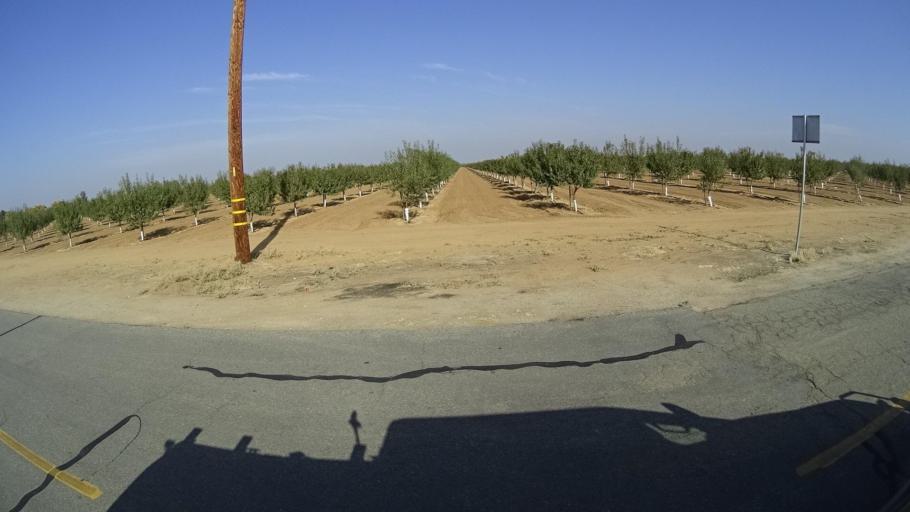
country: US
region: California
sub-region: Kern County
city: McFarland
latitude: 35.6818
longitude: -119.2168
